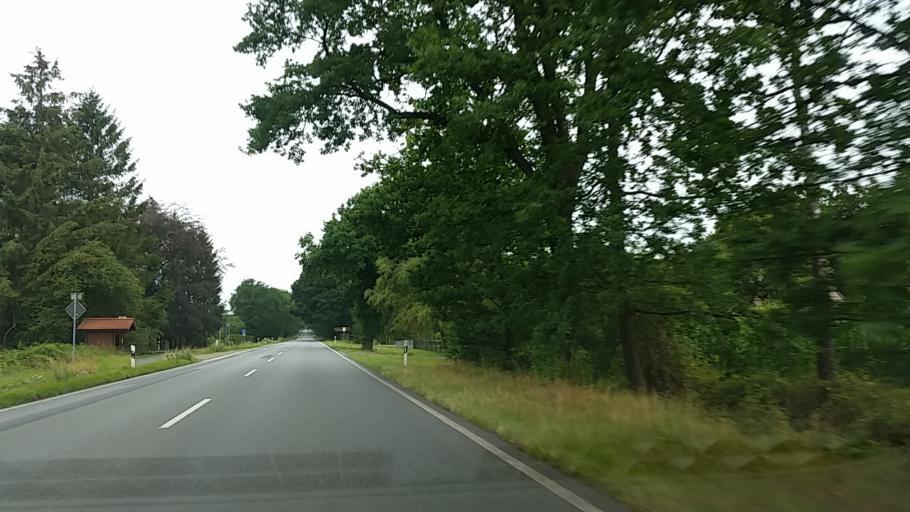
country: DE
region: Lower Saxony
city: Loxstedt
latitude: 53.4792
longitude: 8.6991
